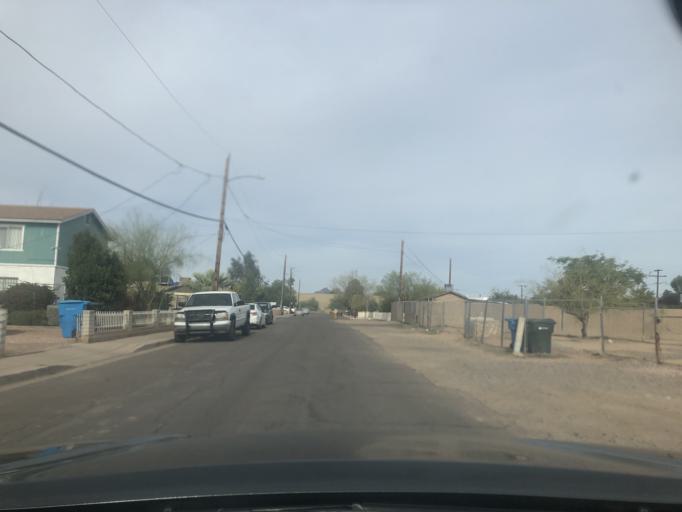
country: US
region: Arizona
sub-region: Maricopa County
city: Phoenix
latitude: 33.4595
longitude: -112.0216
